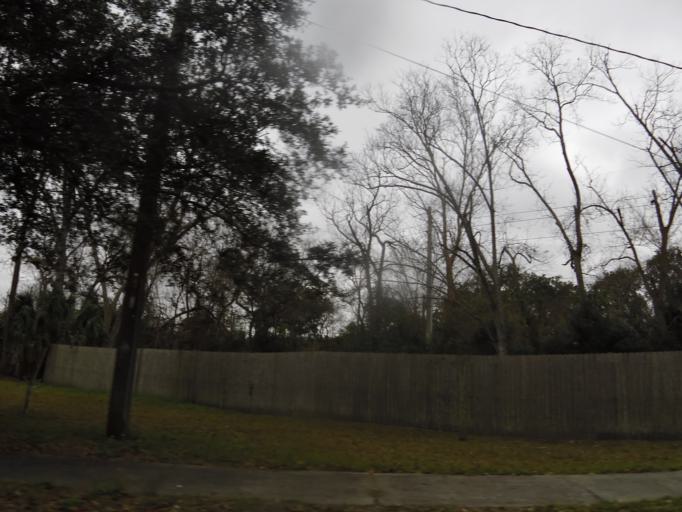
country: US
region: Florida
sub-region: Duval County
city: Jacksonville
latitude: 30.3682
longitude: -81.6867
